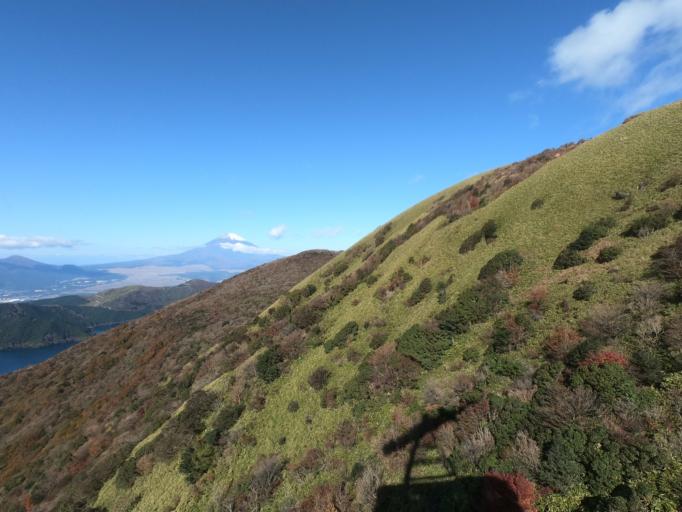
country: JP
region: Kanagawa
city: Hakone
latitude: 35.2232
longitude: 139.0232
